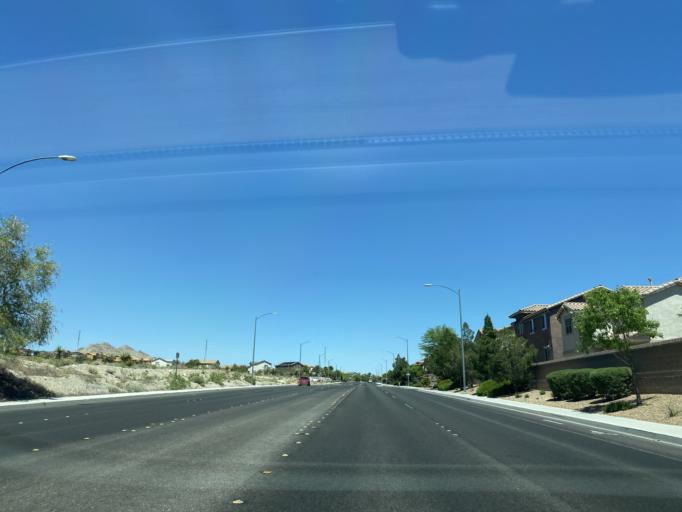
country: US
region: Nevada
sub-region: Clark County
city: Summerlin South
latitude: 36.2340
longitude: -115.3308
